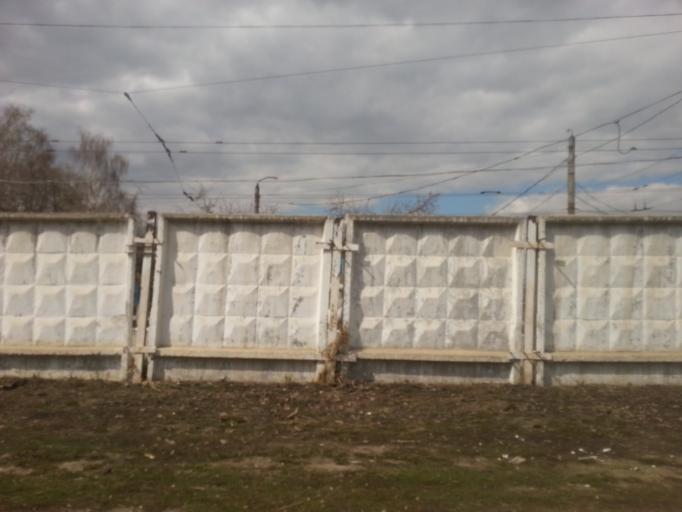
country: RU
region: Altai Krai
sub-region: Gorod Barnaulskiy
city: Barnaul
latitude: 53.3844
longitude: 83.7106
